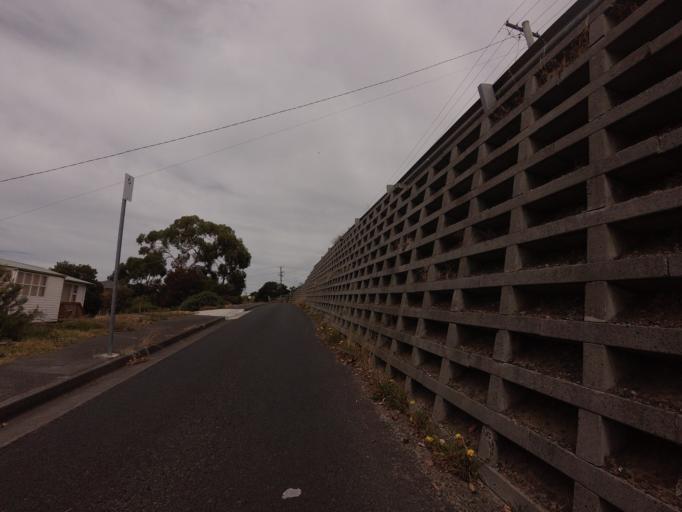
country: AU
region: Tasmania
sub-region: Sorell
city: Sorell
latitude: -42.7953
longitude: 147.5353
